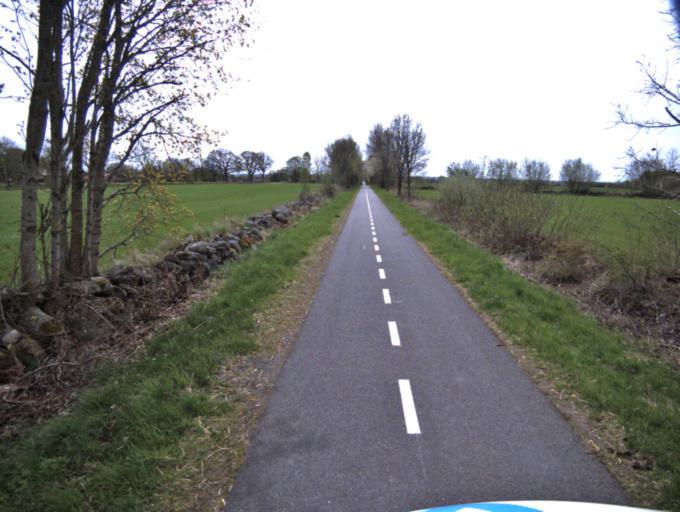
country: SE
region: Skane
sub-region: Kristianstads Kommun
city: Onnestad
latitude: 55.9879
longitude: 14.0306
